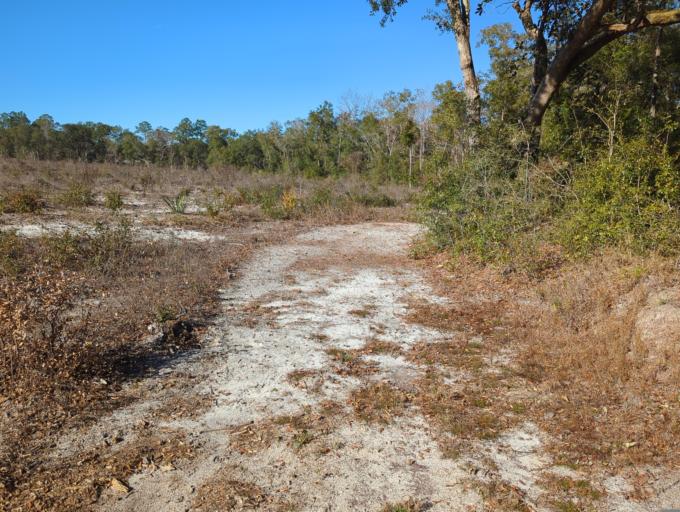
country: US
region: Florida
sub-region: Wakulla County
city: Crawfordville
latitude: 30.1845
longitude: -84.3328
